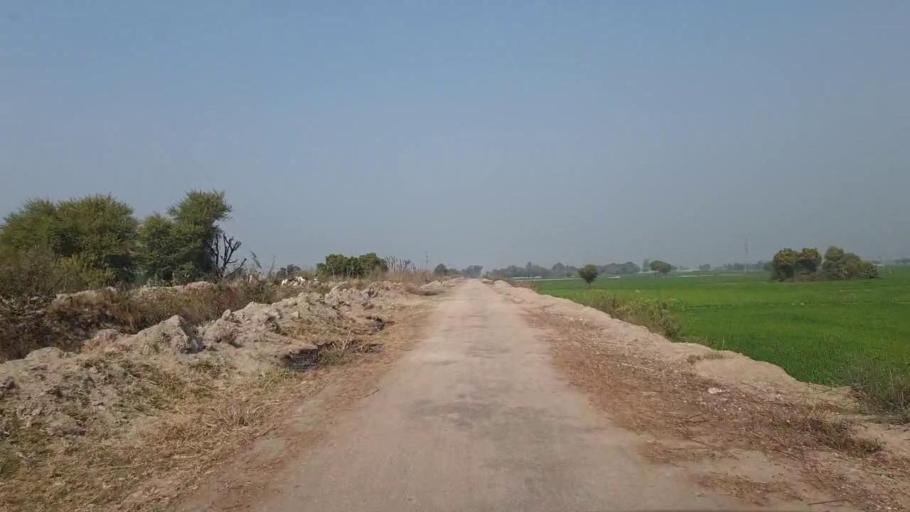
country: PK
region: Sindh
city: Hala
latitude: 25.8360
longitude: 68.4292
